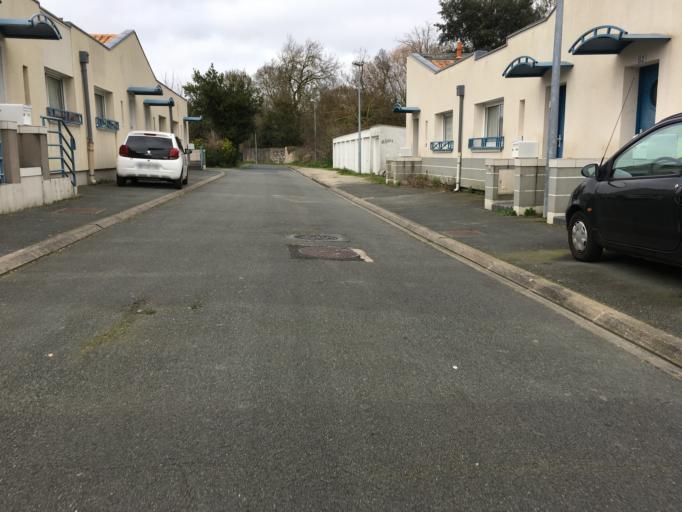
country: FR
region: Poitou-Charentes
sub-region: Departement de la Charente-Maritime
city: La Rochelle
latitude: 46.1765
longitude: -1.1449
